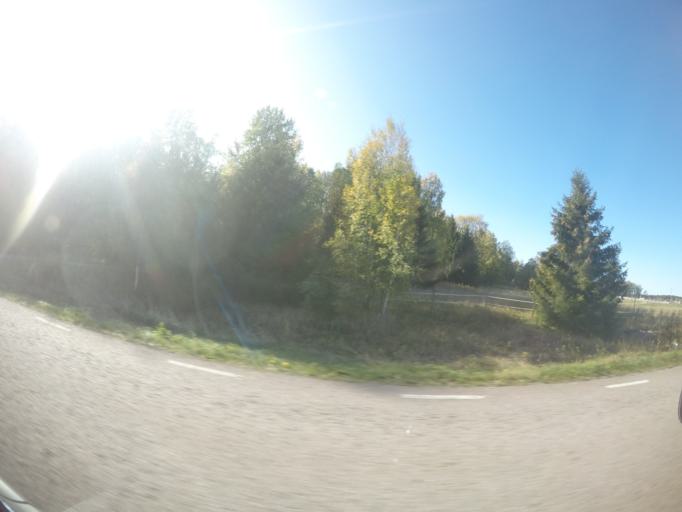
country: SE
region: Soedermanland
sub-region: Eskilstuna Kommun
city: Kvicksund
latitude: 59.5652
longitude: 16.4084
